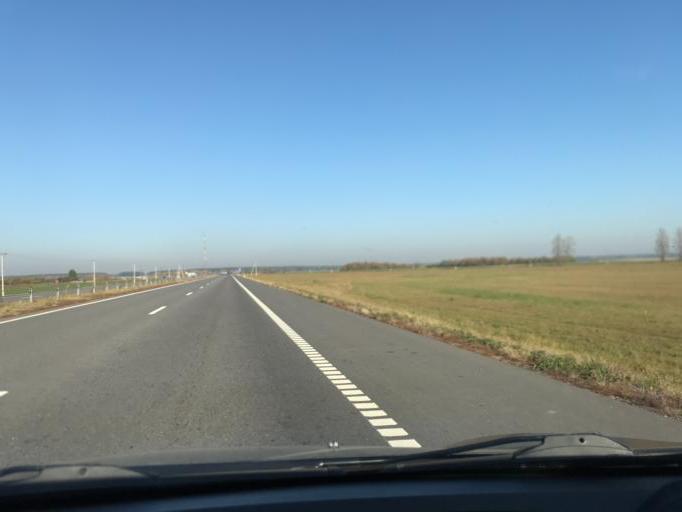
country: BY
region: Mogilev
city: Babruysk
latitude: 53.1675
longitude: 29.3601
